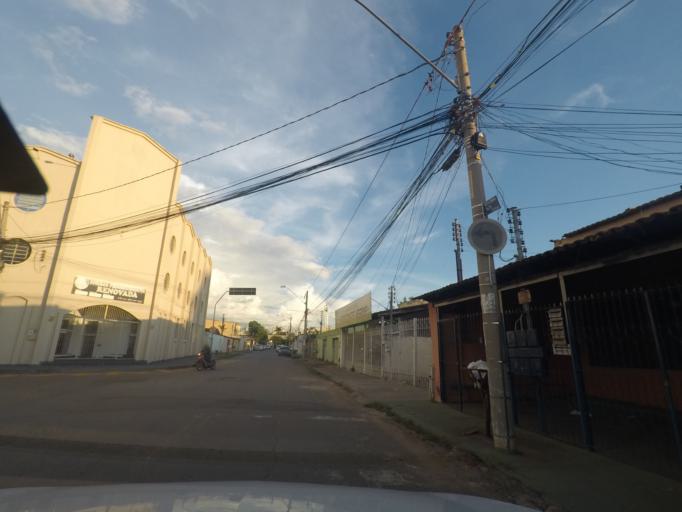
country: BR
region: Goias
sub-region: Goiania
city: Goiania
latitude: -16.6789
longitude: -49.2896
